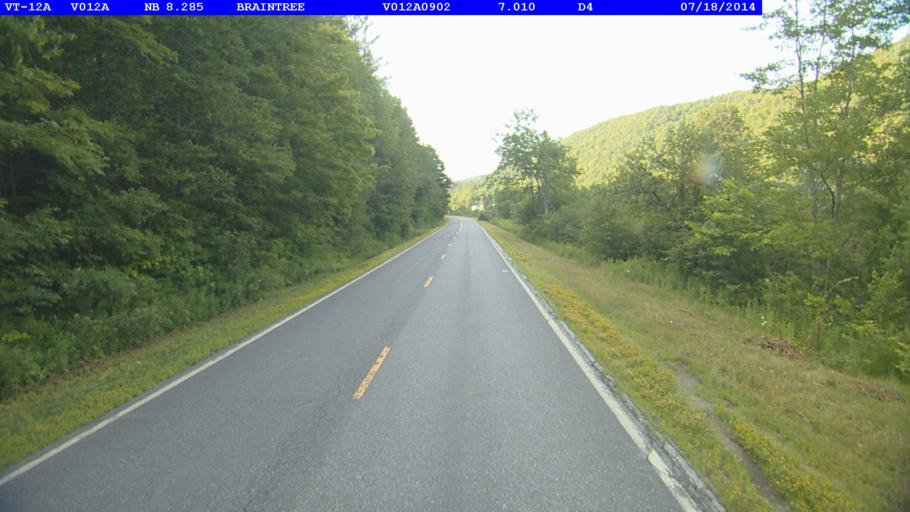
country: US
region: Vermont
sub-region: Orange County
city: Randolph
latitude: 44.0082
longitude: -72.7546
